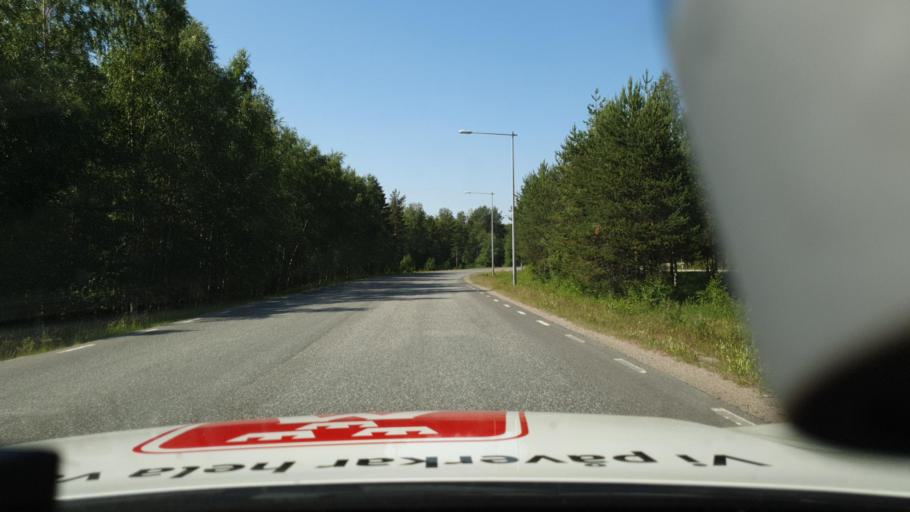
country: SE
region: Norrbotten
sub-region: Kalix Kommun
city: Rolfs
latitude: 65.8676
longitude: 23.1237
